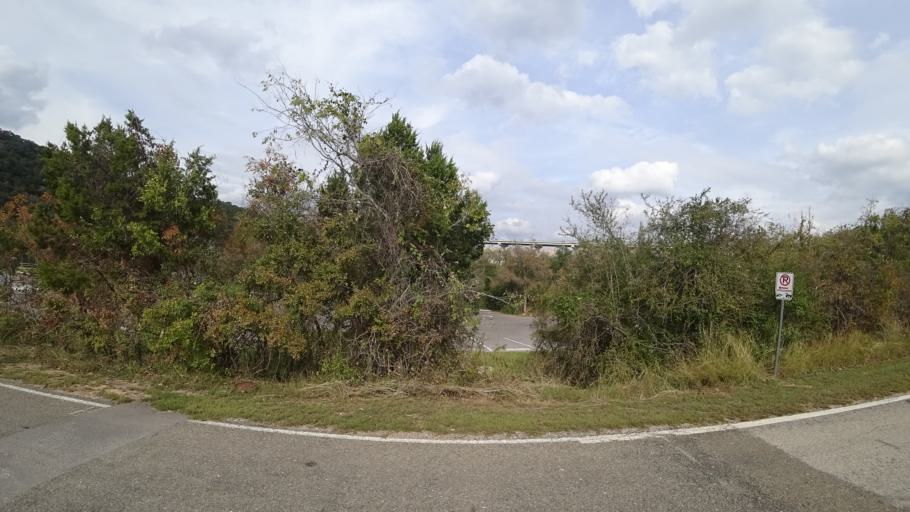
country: US
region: Texas
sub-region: Travis County
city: Hudson Bend
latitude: 30.3874
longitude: -97.9119
